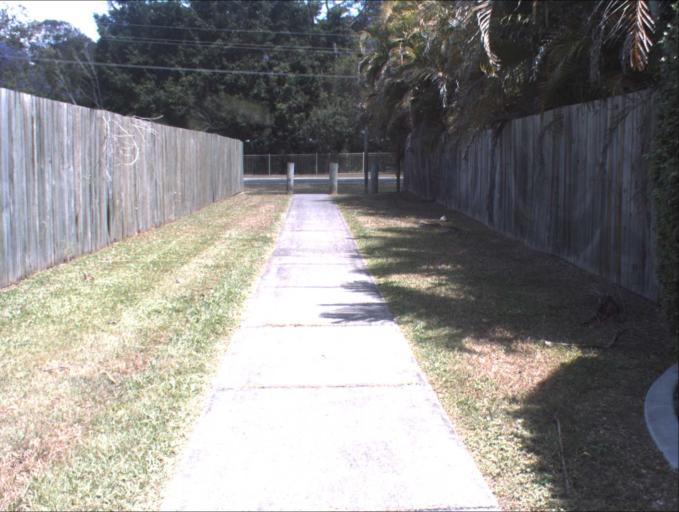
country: AU
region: Queensland
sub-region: Logan
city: Windaroo
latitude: -27.7410
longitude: 153.1835
